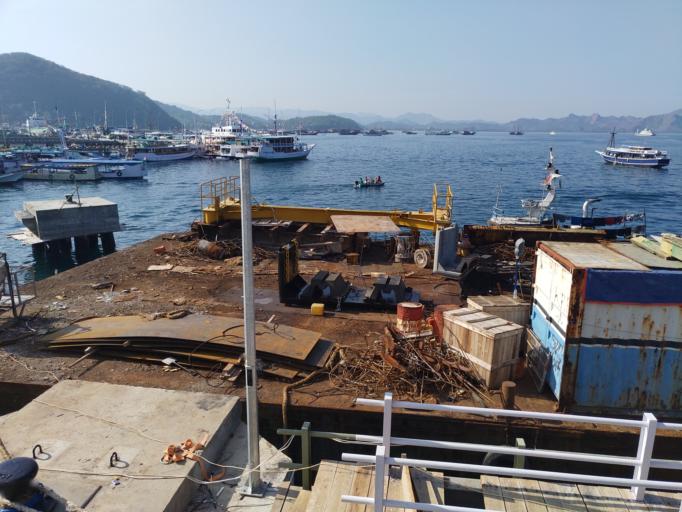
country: ID
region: East Nusa Tenggara
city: Cempa
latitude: -8.4921
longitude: 119.8749
